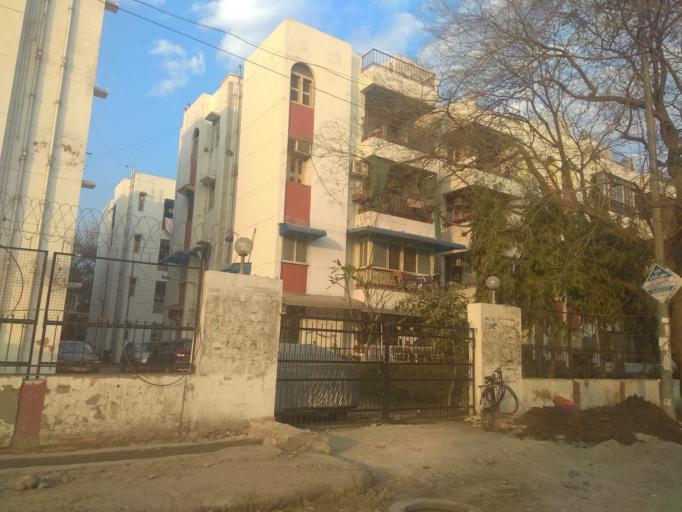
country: IN
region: NCT
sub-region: West Delhi
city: Nangloi Jat
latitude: 28.6355
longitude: 77.0646
